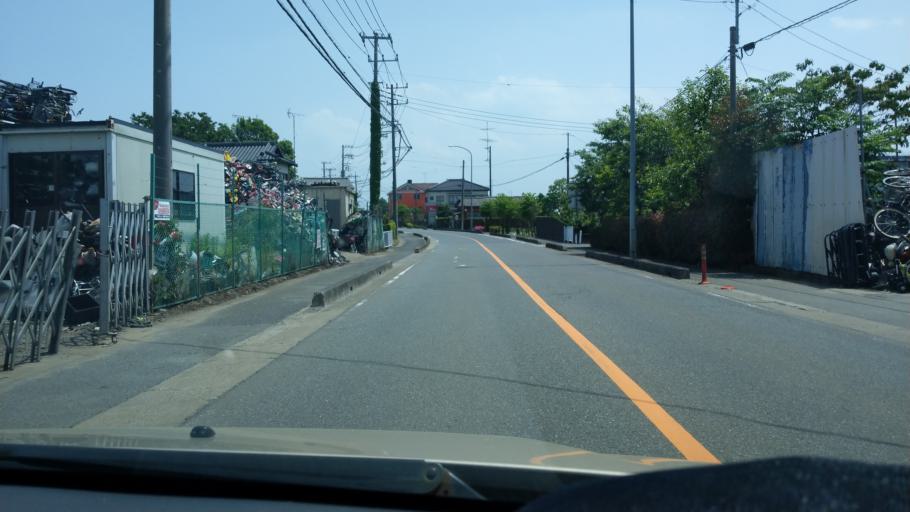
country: JP
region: Saitama
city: Iwatsuki
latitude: 35.9115
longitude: 139.7245
